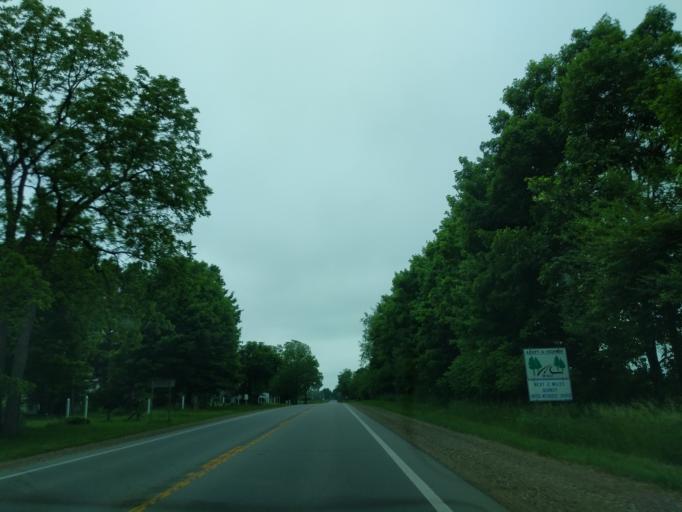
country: US
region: Michigan
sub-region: Hillsdale County
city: Litchfield
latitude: 41.9550
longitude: -84.7791
